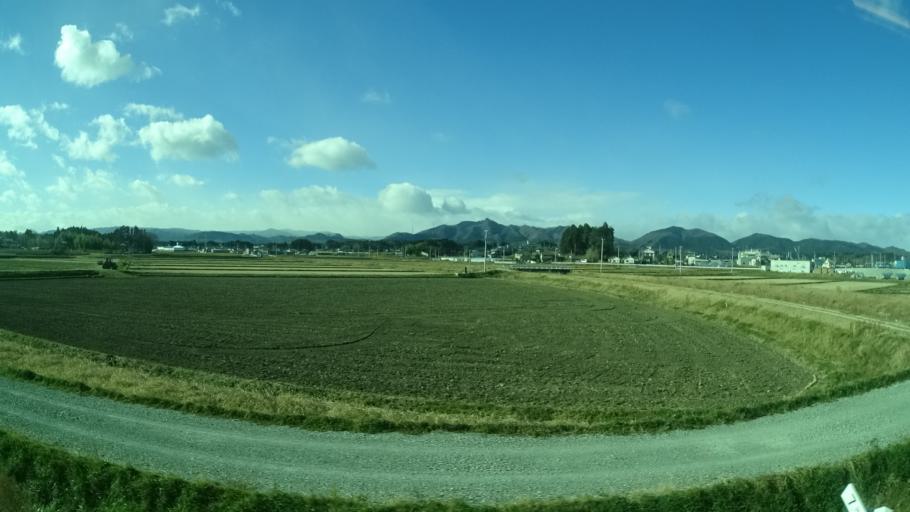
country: JP
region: Miyagi
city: Marumori
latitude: 37.8749
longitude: 140.9272
